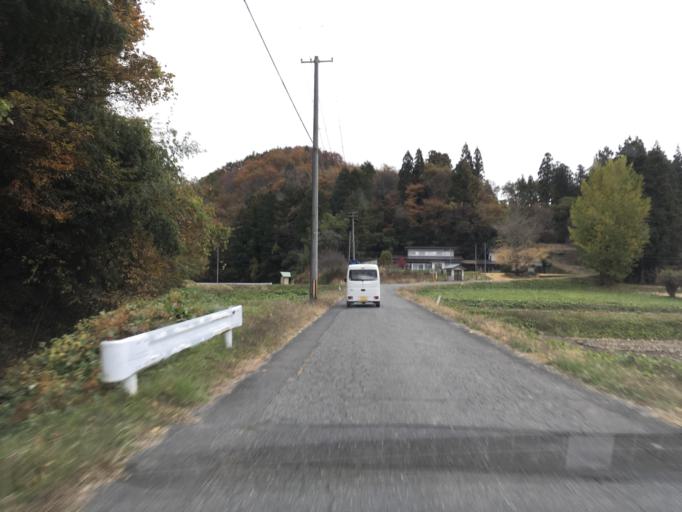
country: JP
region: Iwate
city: Mizusawa
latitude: 39.0476
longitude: 141.3328
